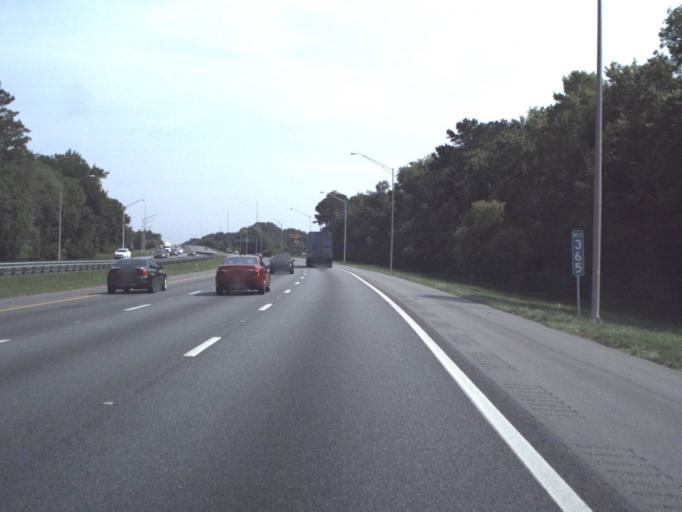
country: US
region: Florida
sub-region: Nassau County
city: Yulee
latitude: 30.5082
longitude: -81.6343
